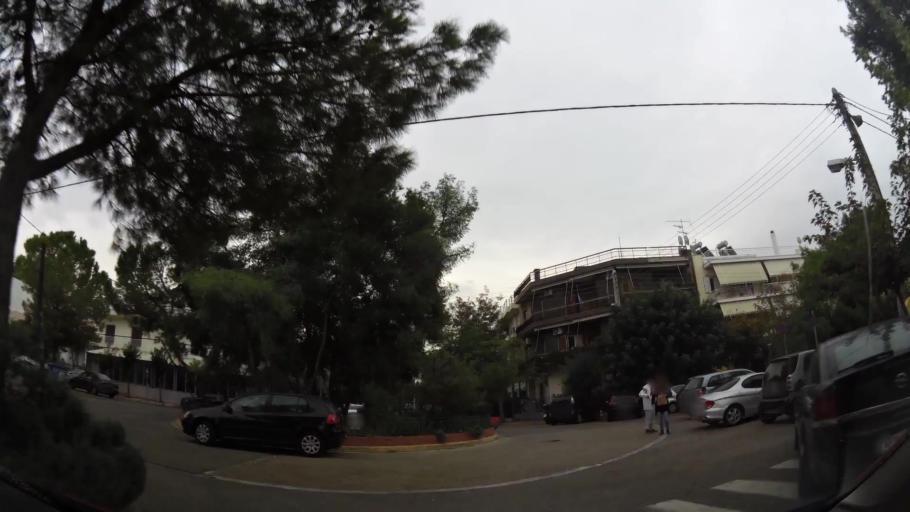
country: GR
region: Attica
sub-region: Nomarchia Athinas
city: Agioi Anargyroi
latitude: 38.0283
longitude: 23.7240
